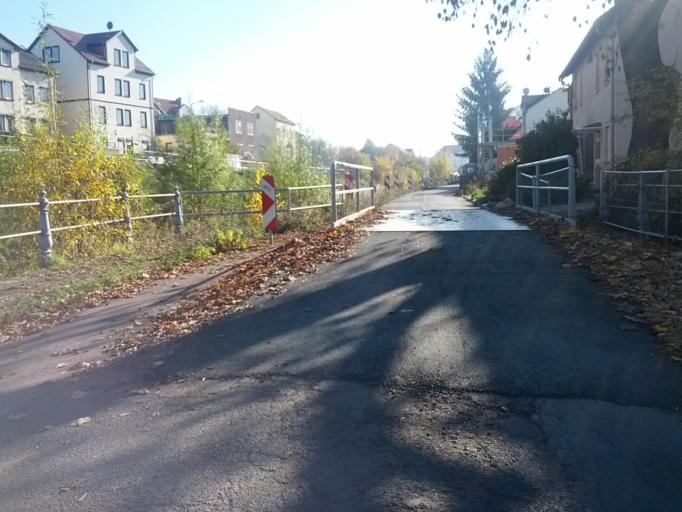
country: DE
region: Thuringia
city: Gotha
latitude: 50.9554
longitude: 10.7085
